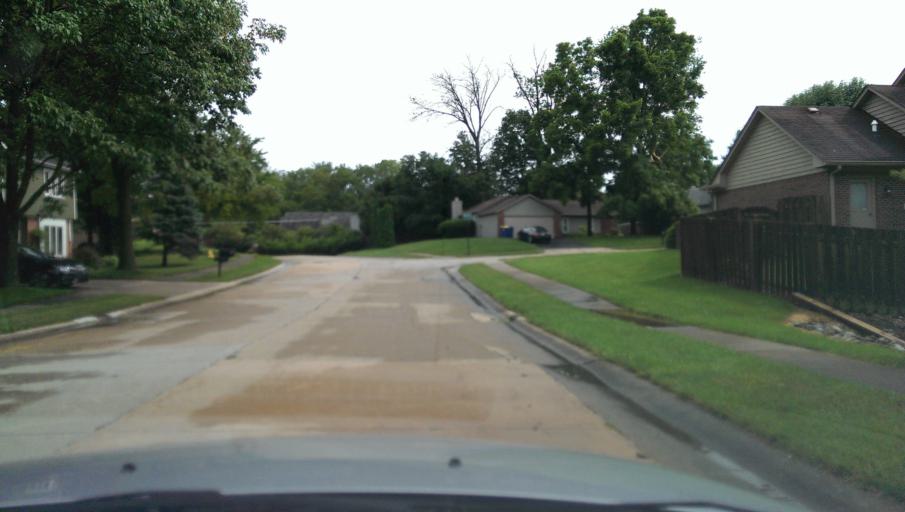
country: US
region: Indiana
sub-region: Hamilton County
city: Carmel
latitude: 39.9936
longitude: -86.1324
